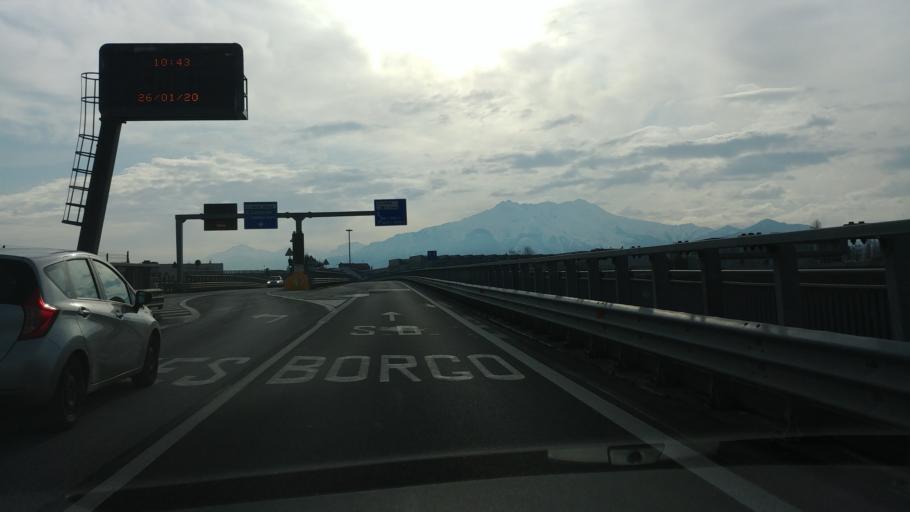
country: IT
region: Piedmont
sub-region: Provincia di Cuneo
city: Cuneo
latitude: 44.3828
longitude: 7.5254
